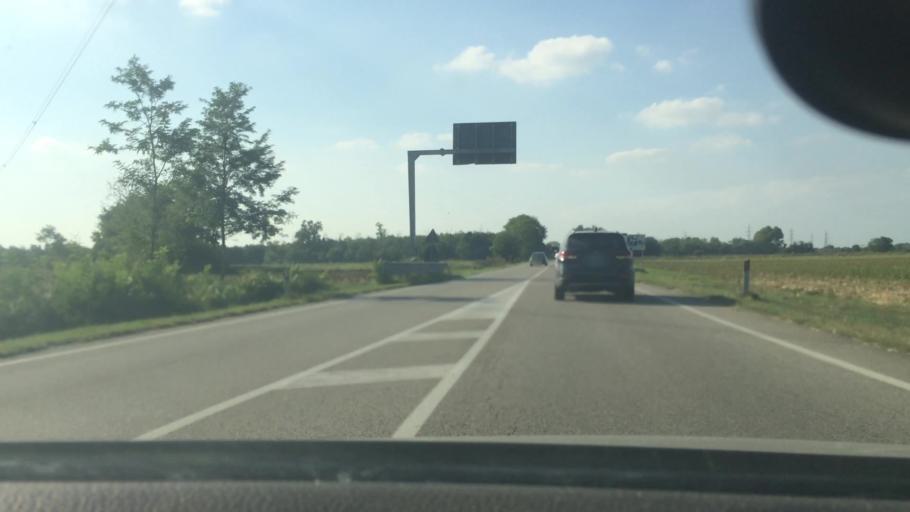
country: IT
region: Lombardy
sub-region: Citta metropolitana di Milano
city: Inveruno
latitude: 45.5253
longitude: 8.8485
